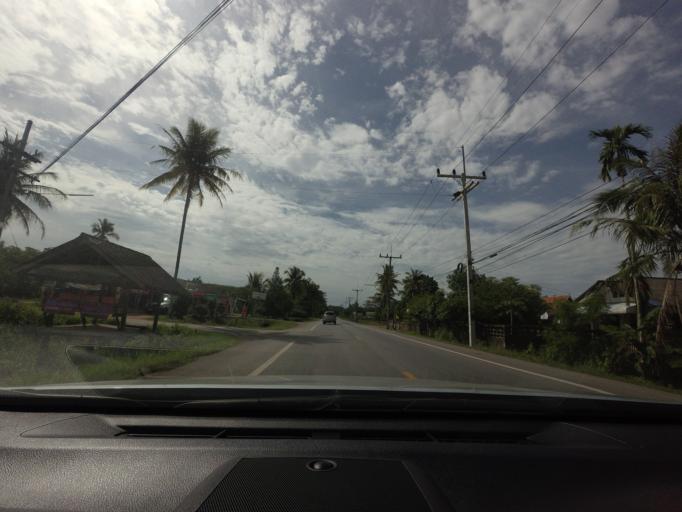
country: TH
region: Songkhla
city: Khlong Hoi Khong
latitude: 6.8902
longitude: 100.4152
